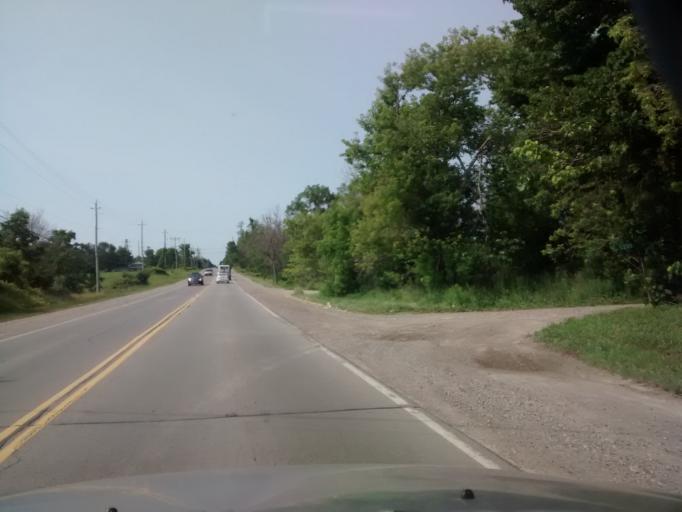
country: CA
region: Ontario
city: Hamilton
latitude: 43.1506
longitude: -79.7919
